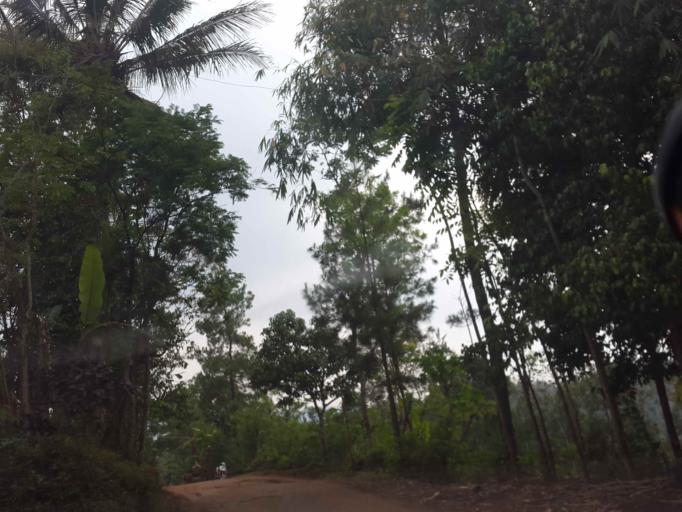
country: ID
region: East Java
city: Krajan Tengah
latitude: -7.9761
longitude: 111.2802
